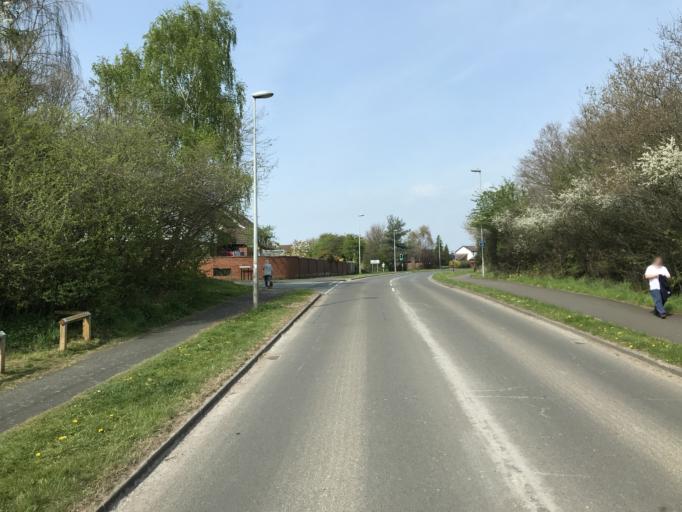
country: GB
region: England
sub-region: Cheshire West and Chester
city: Hoole
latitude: 53.1792
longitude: -2.8599
